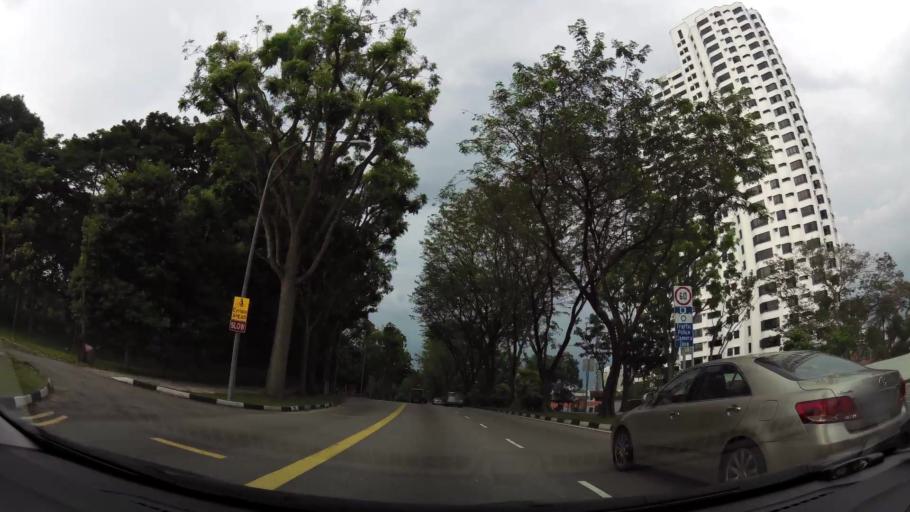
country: SG
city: Singapore
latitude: 1.3601
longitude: 103.8287
